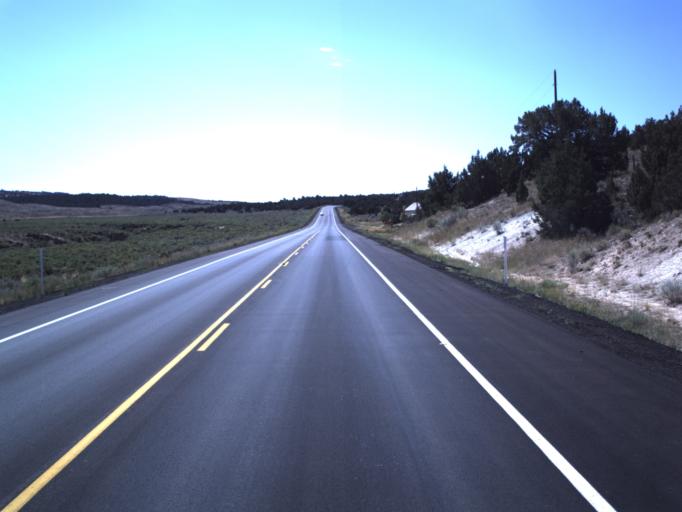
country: US
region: Utah
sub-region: Utah County
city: Eagle Mountain
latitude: 40.0189
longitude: -112.2795
